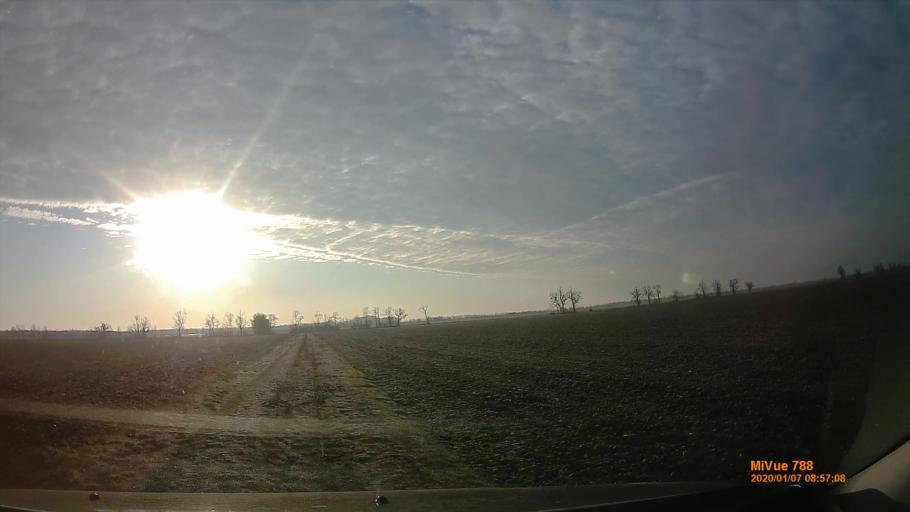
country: HU
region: Gyor-Moson-Sopron
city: Rajka
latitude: 47.9879
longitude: 17.1796
